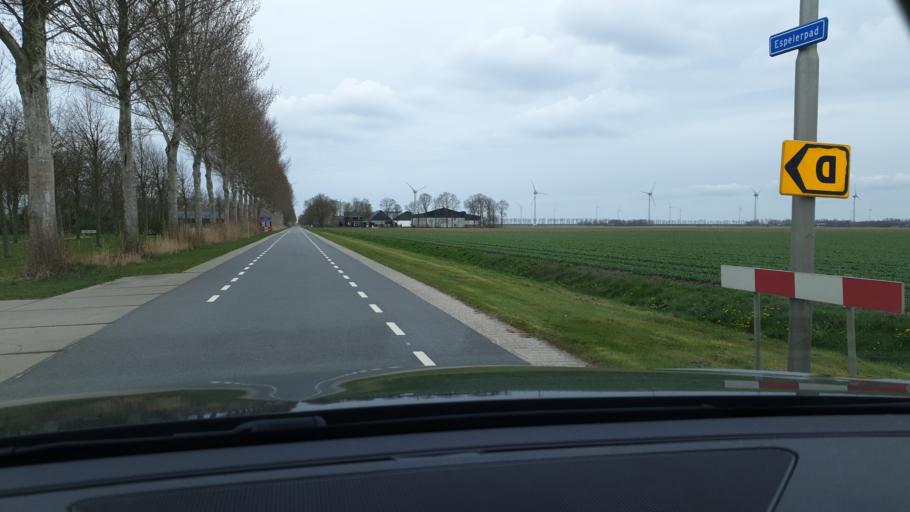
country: NL
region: Flevoland
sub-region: Gemeente Urk
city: Urk
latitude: 52.7252
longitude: 5.6382
